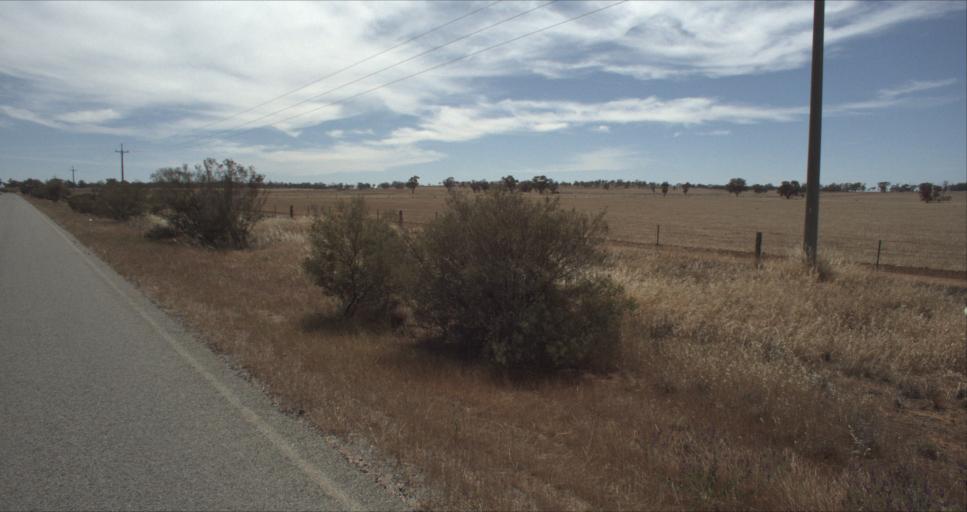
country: AU
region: New South Wales
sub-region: Leeton
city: Leeton
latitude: -34.6255
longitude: 146.4509
